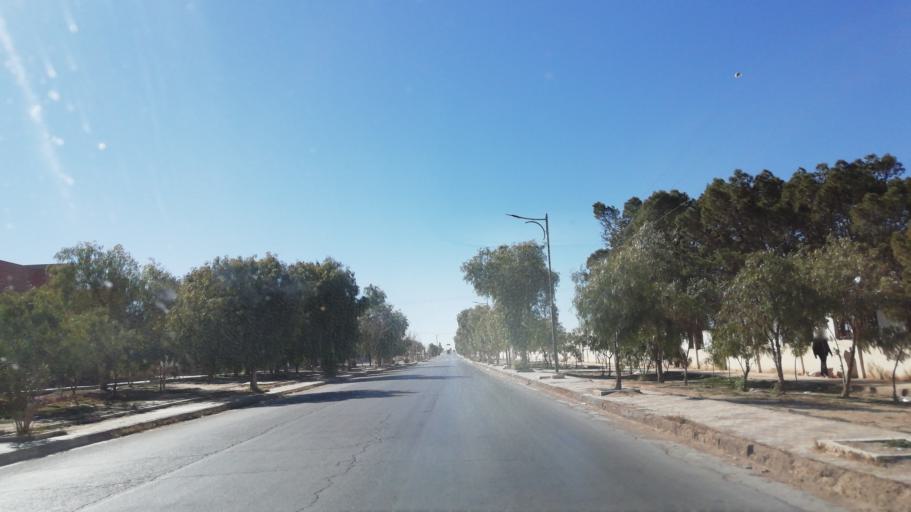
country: DZ
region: Saida
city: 'Ain el Hadjar
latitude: 34.0417
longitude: 0.0825
